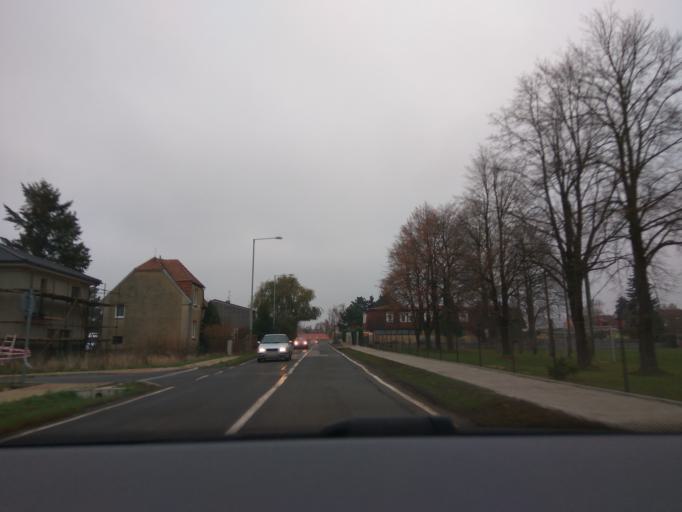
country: CZ
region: Central Bohemia
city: Hovorcovice
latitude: 50.1659
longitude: 14.5235
